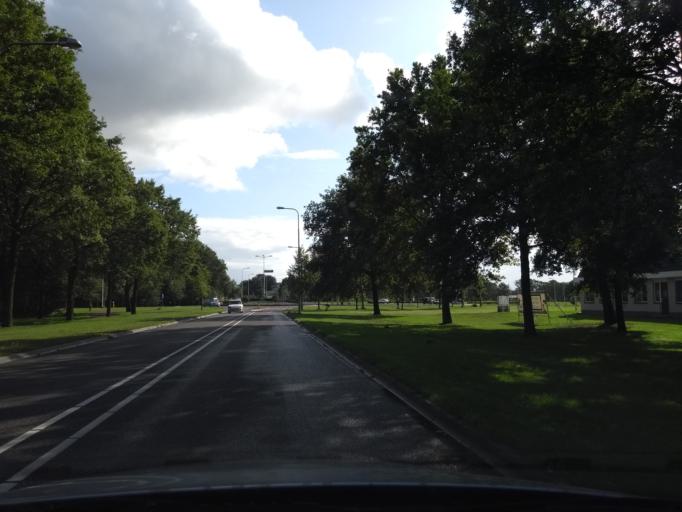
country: NL
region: Overijssel
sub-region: Gemeente Wierden
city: Wierden
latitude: 52.3555
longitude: 6.6064
